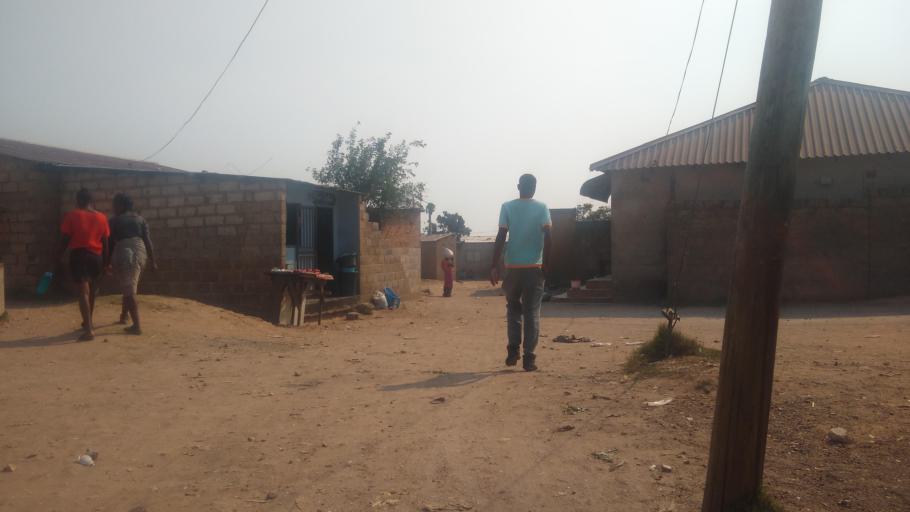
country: ZM
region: Lusaka
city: Lusaka
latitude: -15.4440
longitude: 28.3869
